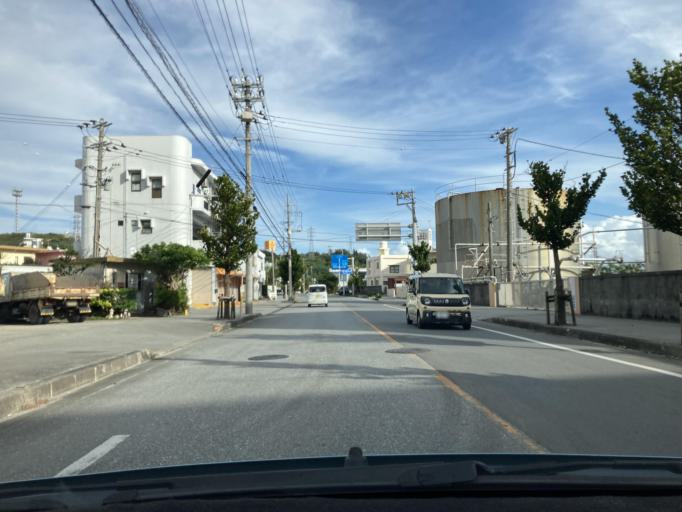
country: JP
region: Okinawa
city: Gushikawa
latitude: 26.3449
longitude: 127.8654
